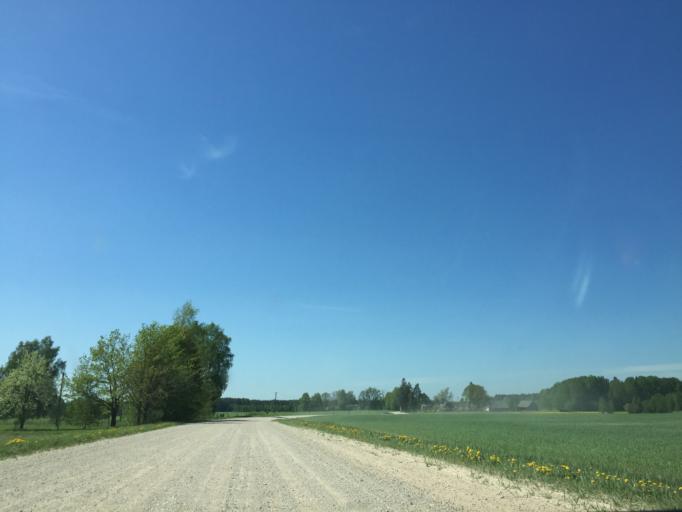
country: LV
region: Kegums
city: Kegums
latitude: 56.8555
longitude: 24.7362
